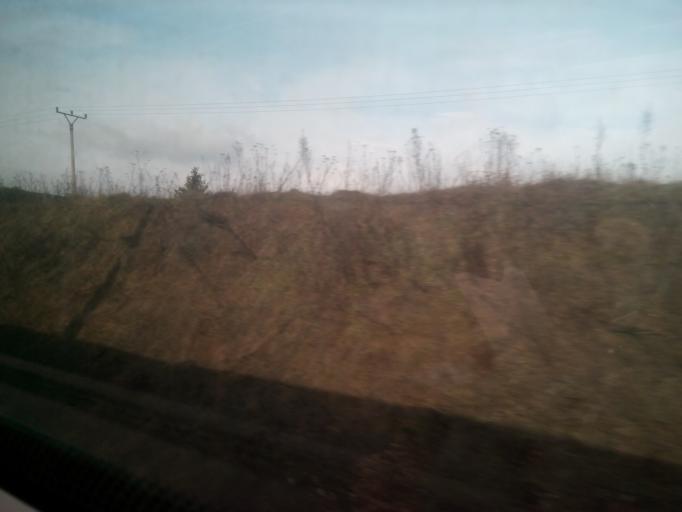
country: SK
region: Presovsky
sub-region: Okres Poprad
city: Strba
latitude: 49.0611
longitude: 19.9640
